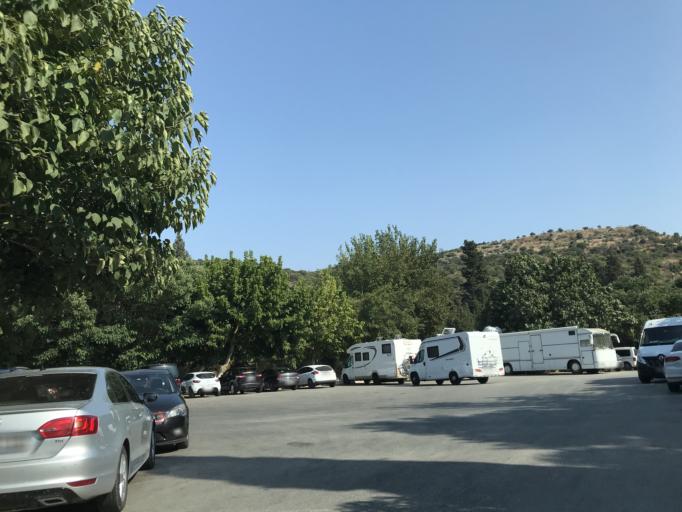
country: TR
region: Izmir
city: Selcuk
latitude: 37.9441
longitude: 27.3419
